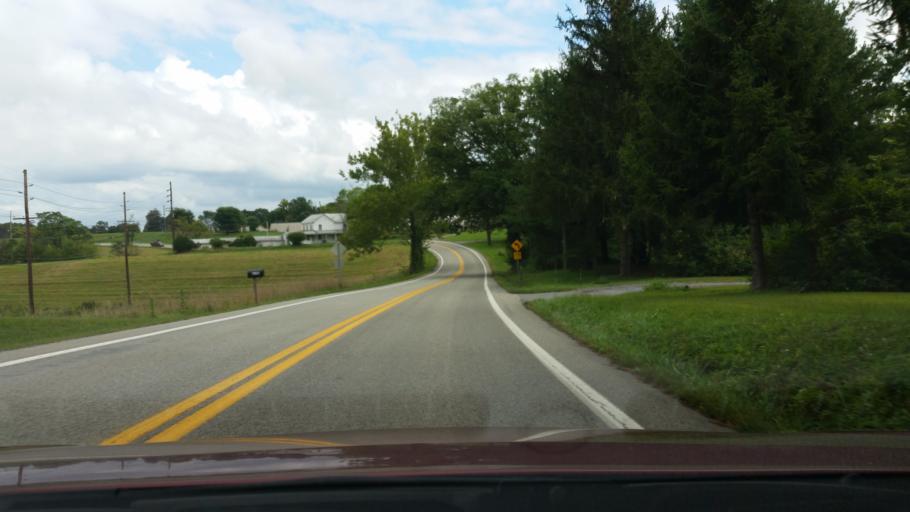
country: US
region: Maryland
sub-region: Washington County
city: Hancock
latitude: 39.6370
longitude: -78.1370
